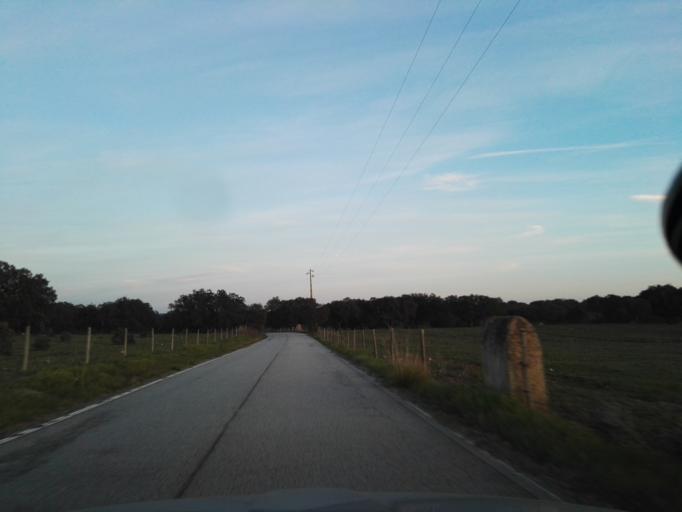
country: PT
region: Evora
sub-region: Montemor-O-Novo
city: Montemor-o-Novo
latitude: 38.7595
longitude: -8.1718
